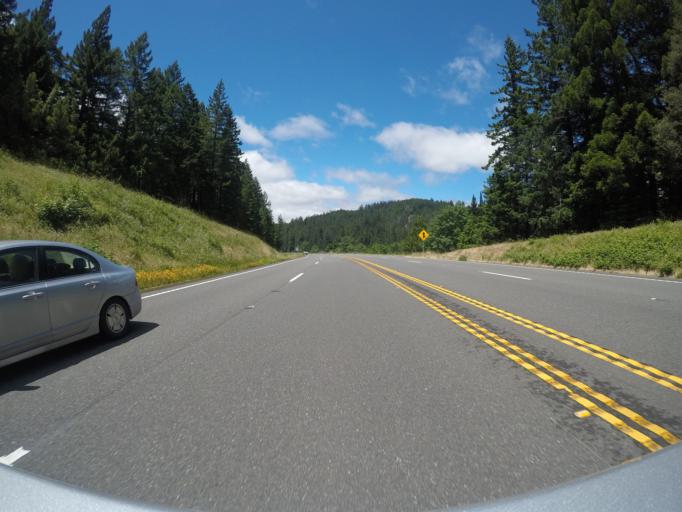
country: US
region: California
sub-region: Humboldt County
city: Redway
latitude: 40.2517
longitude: -123.8321
